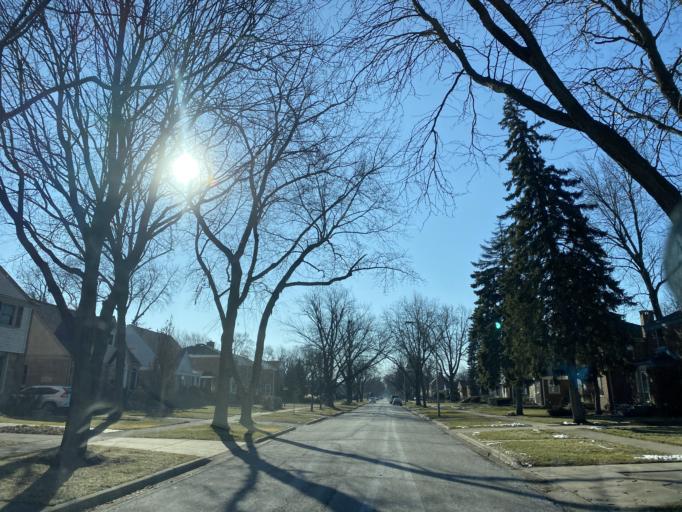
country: US
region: Illinois
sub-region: Cook County
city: Westchester
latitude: 41.8579
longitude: -87.8700
